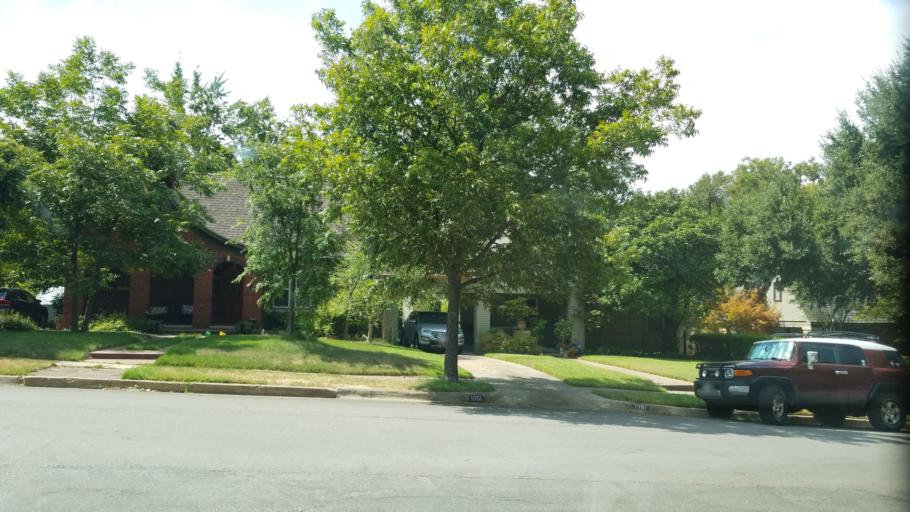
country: US
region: Texas
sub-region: Dallas County
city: Dallas
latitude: 32.7571
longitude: -96.8390
